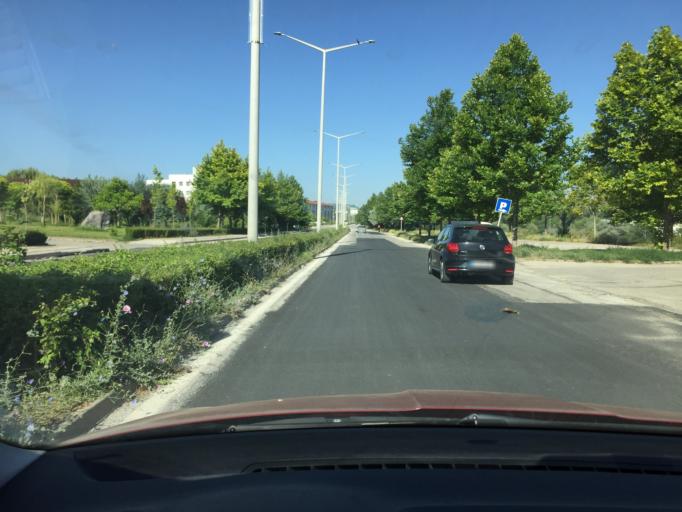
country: TR
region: Eskisehir
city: Eskisehir
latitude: 39.7529
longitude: 30.4826
